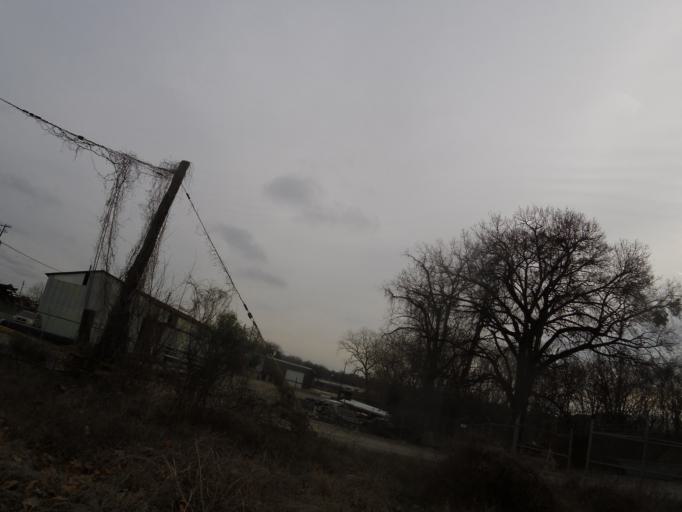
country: US
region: Alabama
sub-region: Montgomery County
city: Montgomery
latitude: 32.3853
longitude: -86.3109
